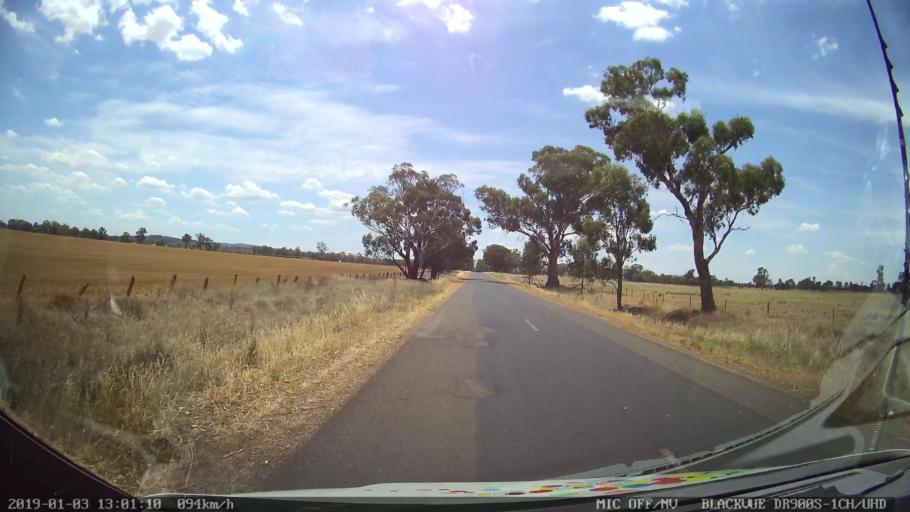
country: AU
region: New South Wales
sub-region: Cabonne
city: Canowindra
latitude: -33.6266
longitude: 148.4143
